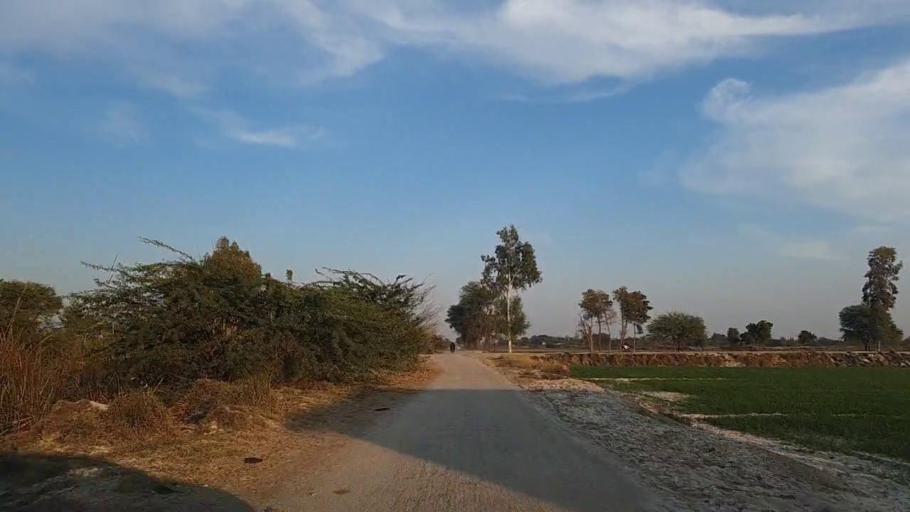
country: PK
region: Sindh
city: Bandhi
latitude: 26.5980
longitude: 68.3521
